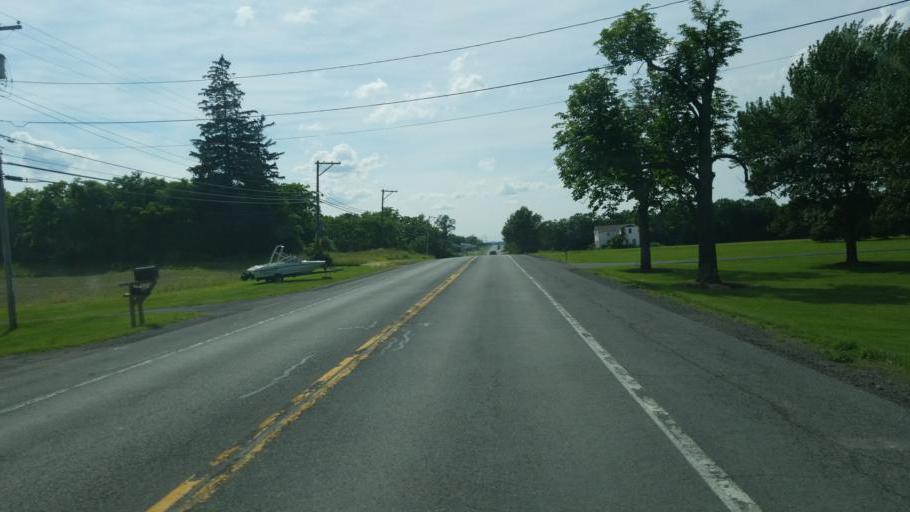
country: US
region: New York
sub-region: Ontario County
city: Canandaigua
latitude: 42.8622
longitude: -77.2034
